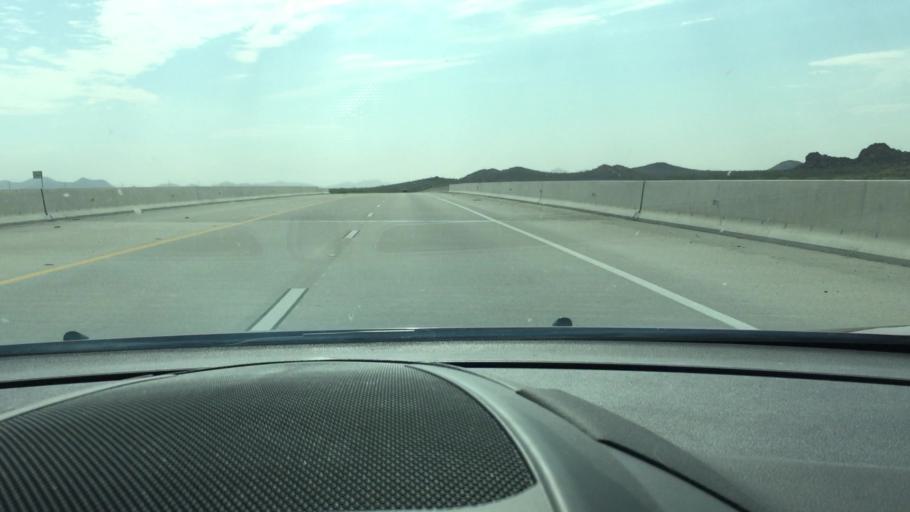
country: US
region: Arizona
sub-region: Maricopa County
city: Anthem
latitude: 33.7788
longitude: -112.2244
